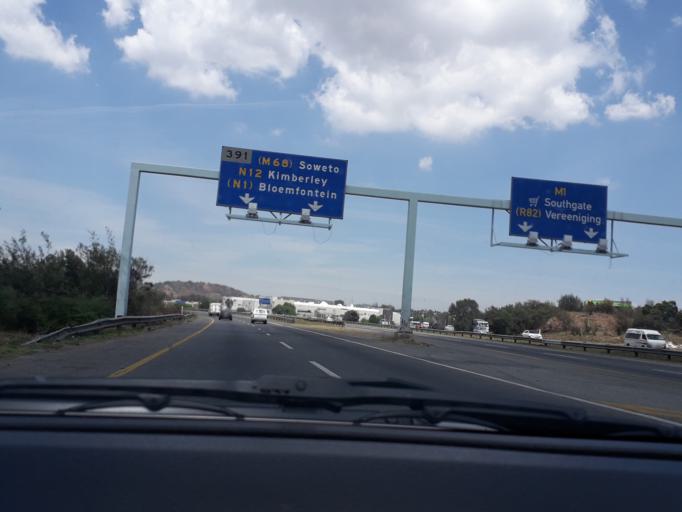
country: ZA
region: Gauteng
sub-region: City of Johannesburg Metropolitan Municipality
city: Johannesburg
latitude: -26.2596
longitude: 27.9872
